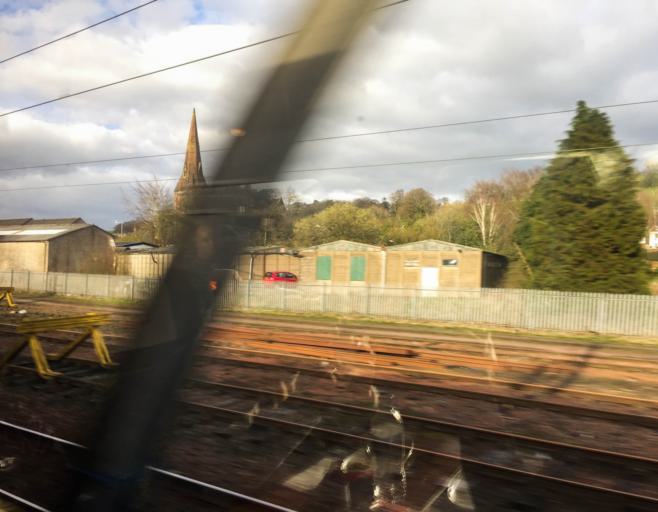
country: GB
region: Scotland
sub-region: Dumfries and Galloway
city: Lockerbie
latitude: 55.1212
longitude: -3.3533
